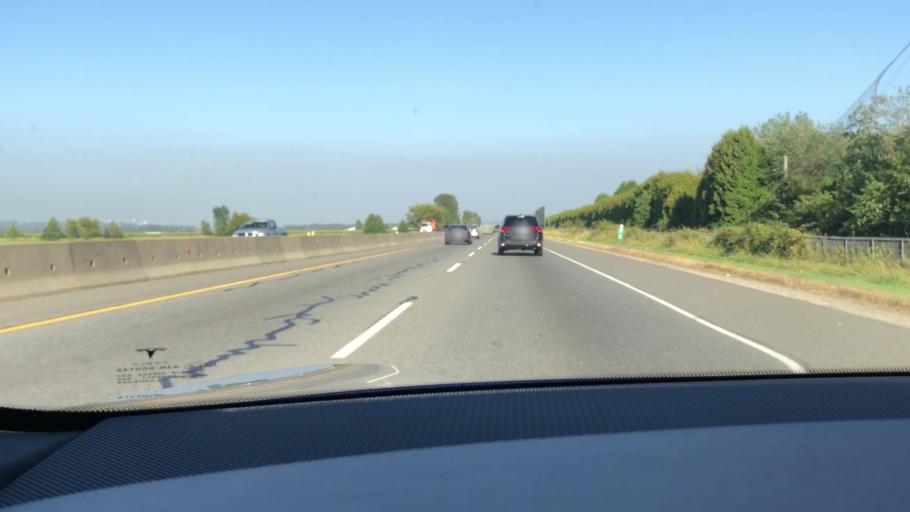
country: CA
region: British Columbia
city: Richmond
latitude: 49.1769
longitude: -123.0407
